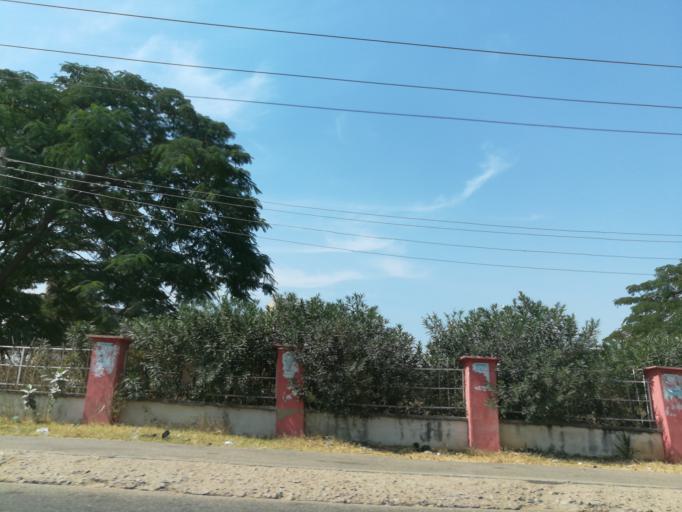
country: NG
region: Kano
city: Kano
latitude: 12.0245
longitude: 8.5155
